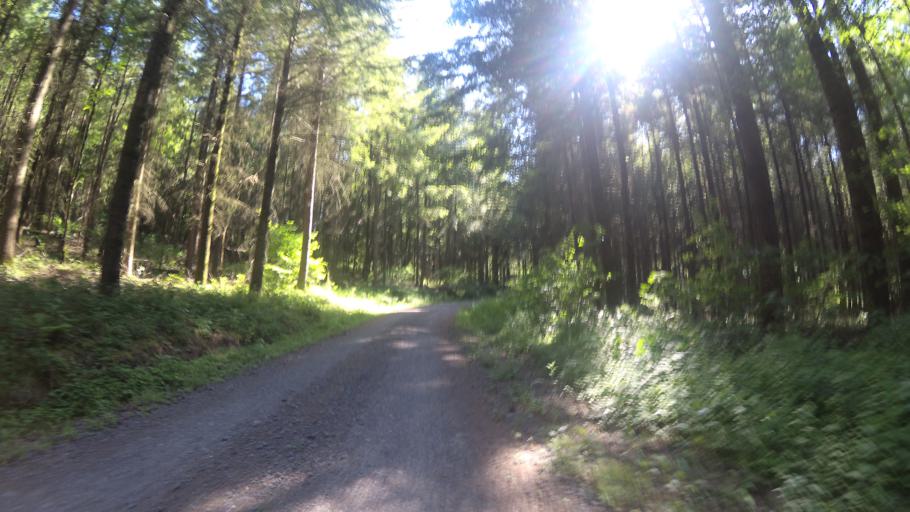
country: DE
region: Saarland
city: Mainzweiler
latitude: 49.4479
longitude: 7.0979
